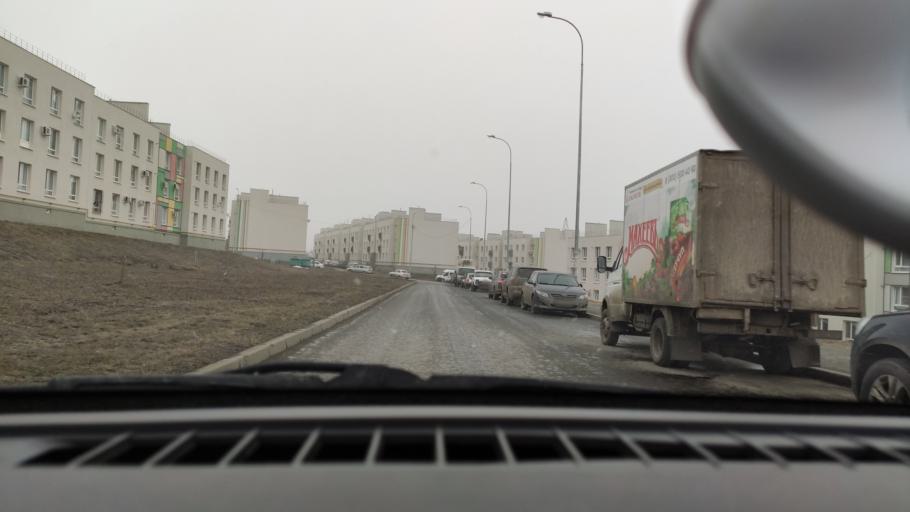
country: RU
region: Samara
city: Petra-Dubrava
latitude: 53.3250
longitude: 50.3160
